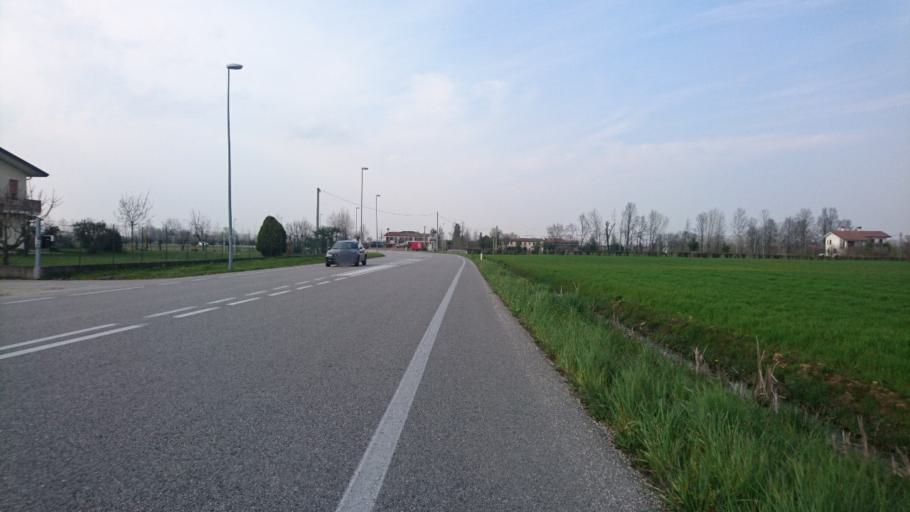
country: IT
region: Veneto
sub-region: Provincia di Padova
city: San Biagio
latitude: 45.3823
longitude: 11.7295
